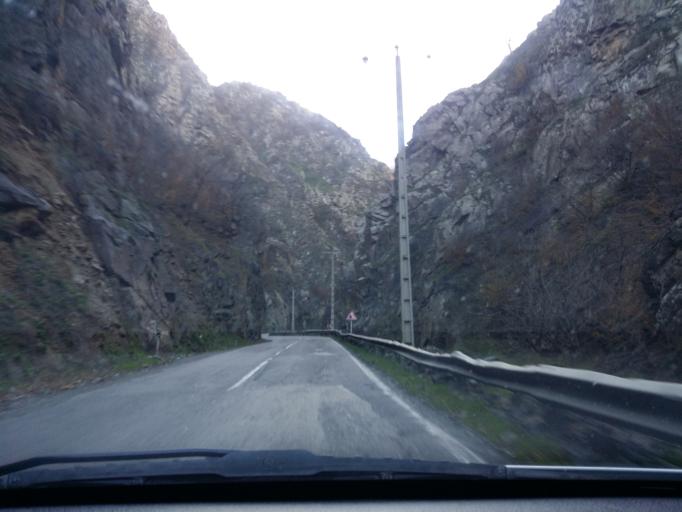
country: IR
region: Mazandaran
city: Chalus
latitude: 36.2828
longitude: 51.2424
